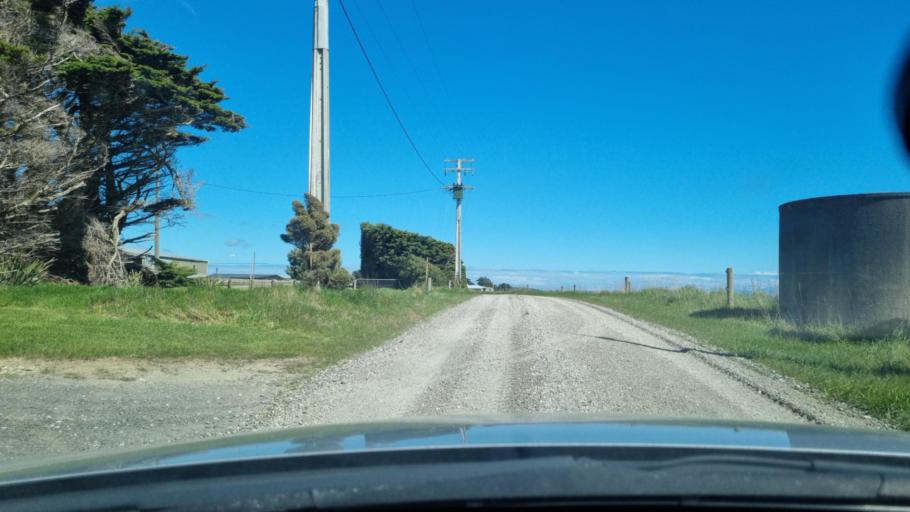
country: NZ
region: Southland
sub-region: Invercargill City
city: Invercargill
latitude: -46.3939
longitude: 168.2581
